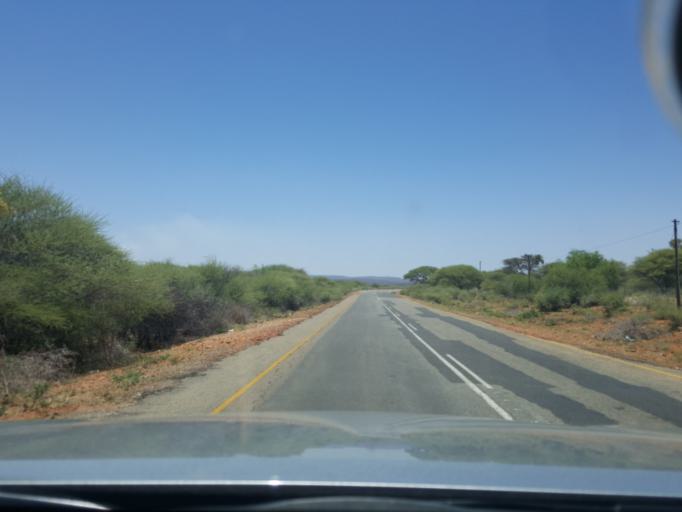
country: ZA
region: North-West
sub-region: Ngaka Modiri Molema District Municipality
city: Zeerust
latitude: -25.3243
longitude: 25.9386
